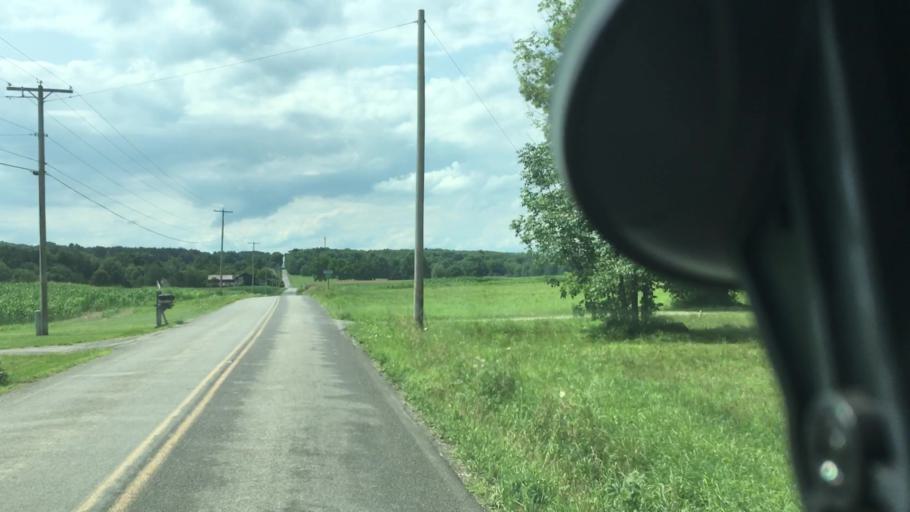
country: US
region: Pennsylvania
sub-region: Mercer County
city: Reynolds Heights
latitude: 41.3096
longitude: -80.3859
